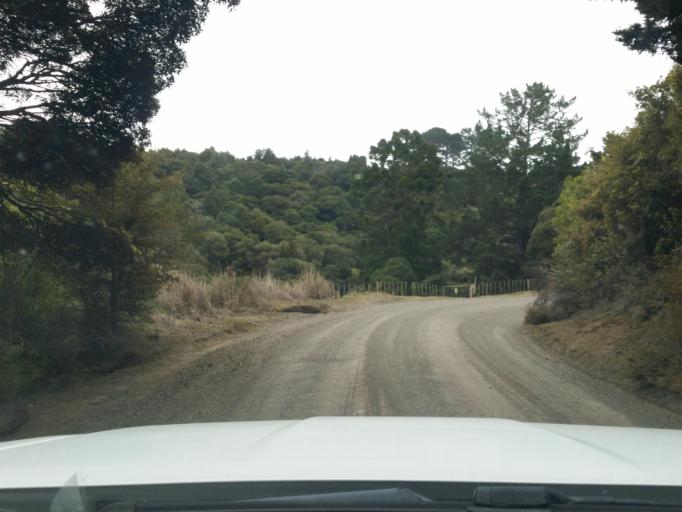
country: NZ
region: Northland
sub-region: Kaipara District
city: Dargaville
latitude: -35.7127
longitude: 173.6324
